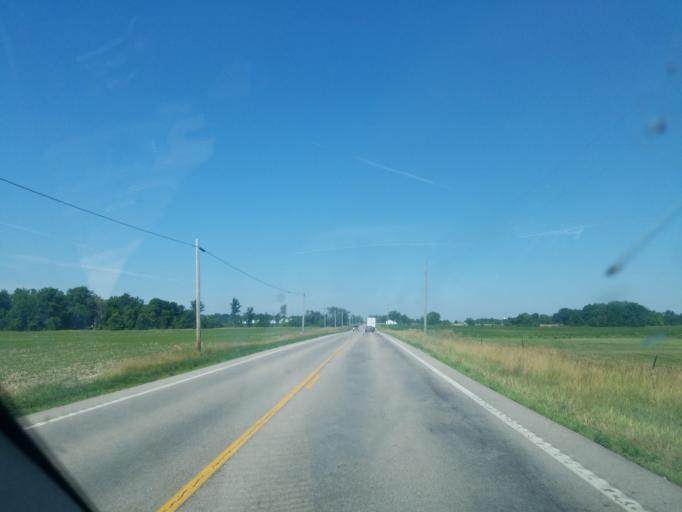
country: US
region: Ohio
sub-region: Shelby County
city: Jackson Center
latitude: 40.4394
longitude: -84.0085
